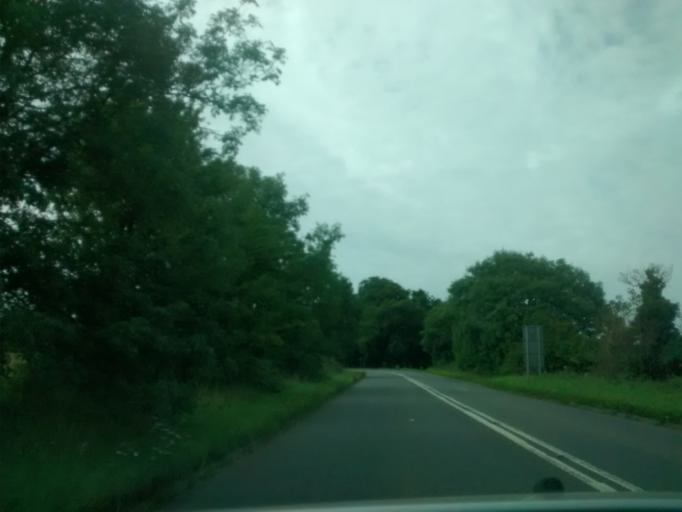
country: GB
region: England
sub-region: South Gloucestershire
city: Horton
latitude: 51.5259
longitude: -2.3428
